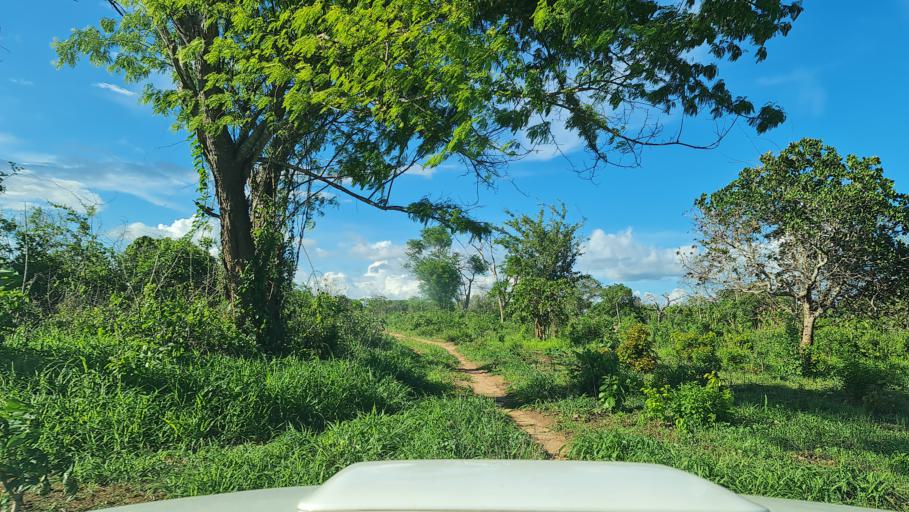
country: MZ
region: Nampula
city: Ilha de Mocambique
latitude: -15.2664
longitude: 40.1862
